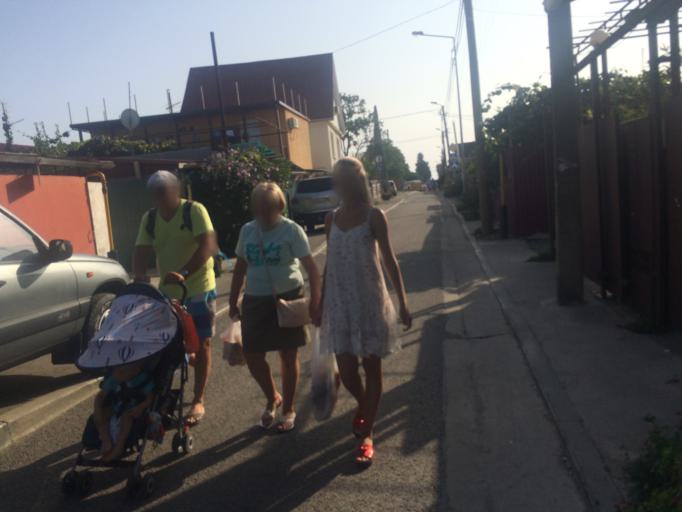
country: RU
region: Krasnodarskiy
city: Adler
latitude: 43.3945
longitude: 39.9796
